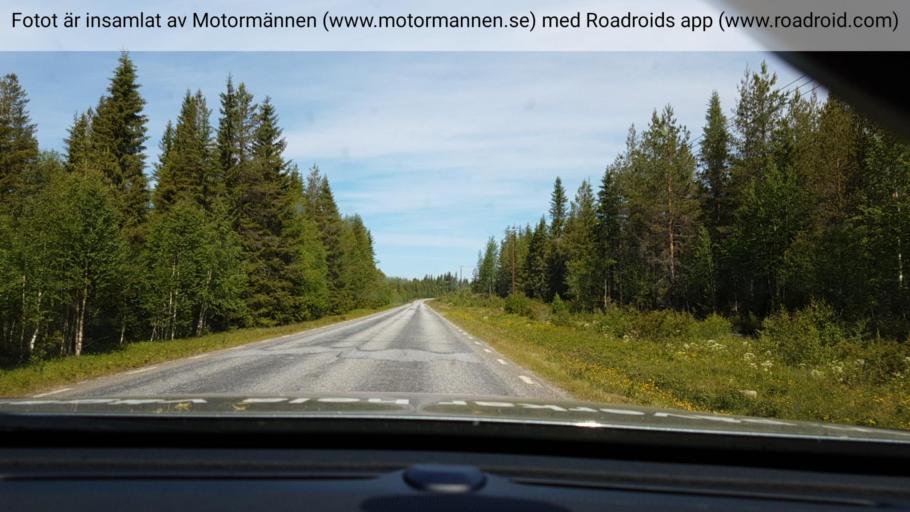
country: SE
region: Vaesterbotten
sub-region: Vilhelmina Kommun
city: Sjoberg
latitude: 64.5017
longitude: 15.9306
